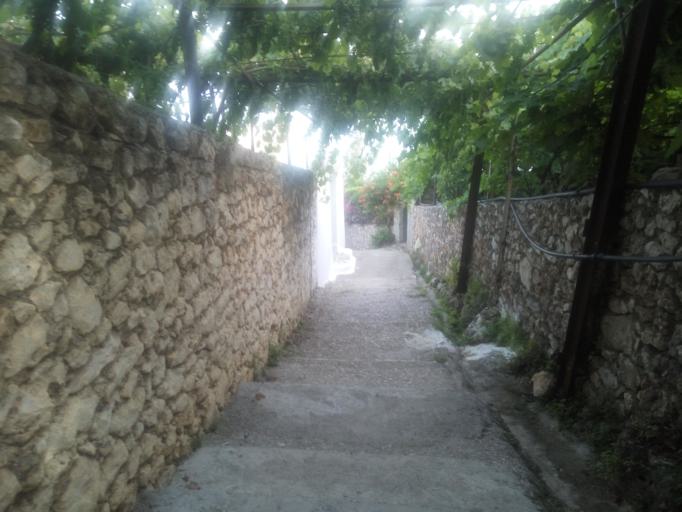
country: AL
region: Vlore
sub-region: Rrethi i Vlores
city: Himare
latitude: 40.0527
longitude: 19.8300
